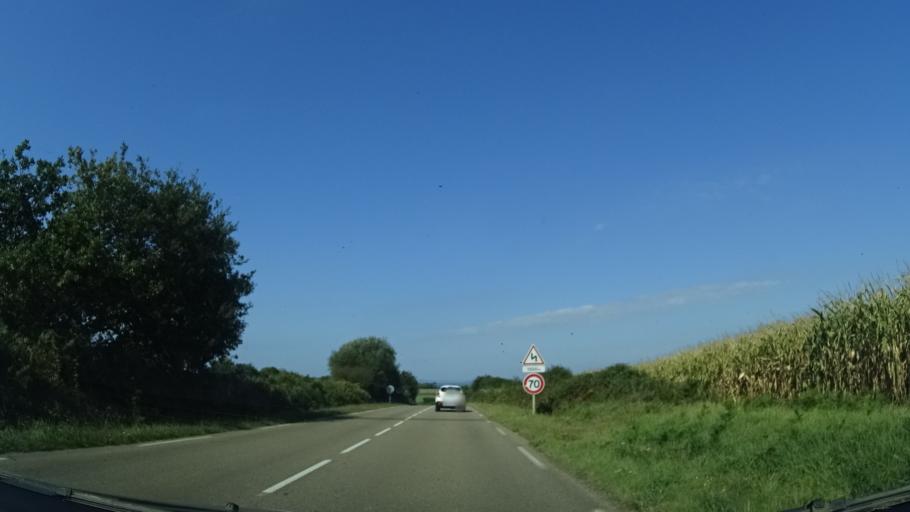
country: FR
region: Brittany
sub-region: Departement du Finistere
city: Douarnenez
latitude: 48.0928
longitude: -4.2797
